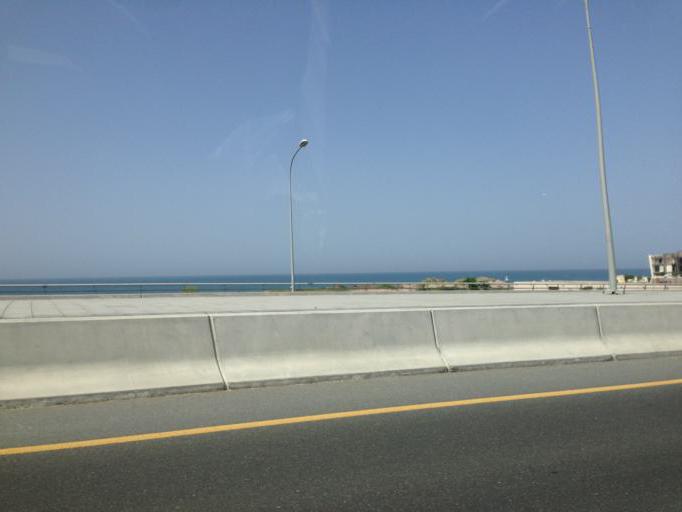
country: OM
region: Muhafazat Masqat
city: Bawshar
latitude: 23.6082
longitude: 58.3119
